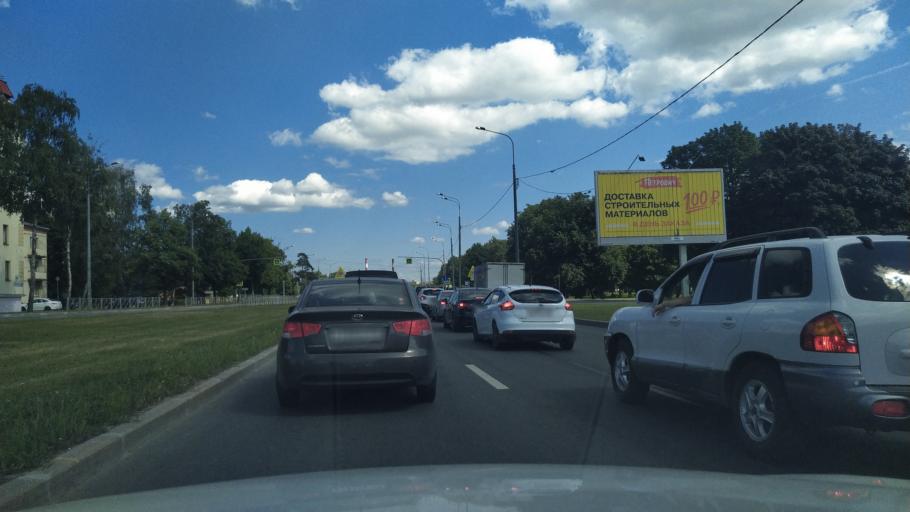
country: RU
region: Leningrad
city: Kalininskiy
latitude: 59.9948
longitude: 30.4084
